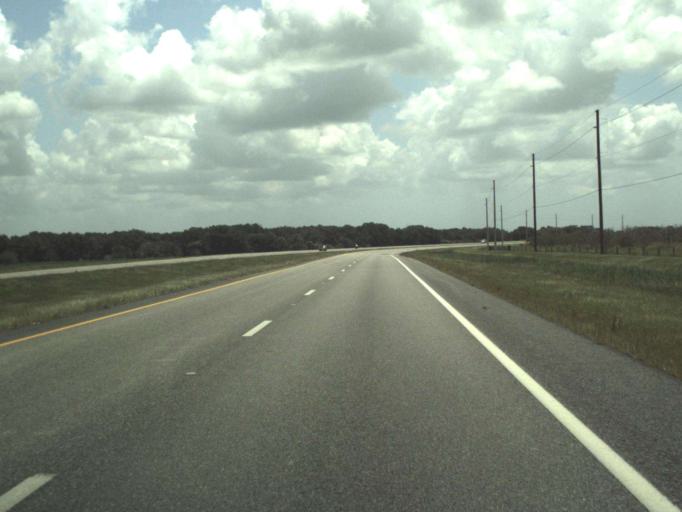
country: US
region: Florida
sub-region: Saint Lucie County
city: Fort Pierce South
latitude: 27.3750
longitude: -80.5760
